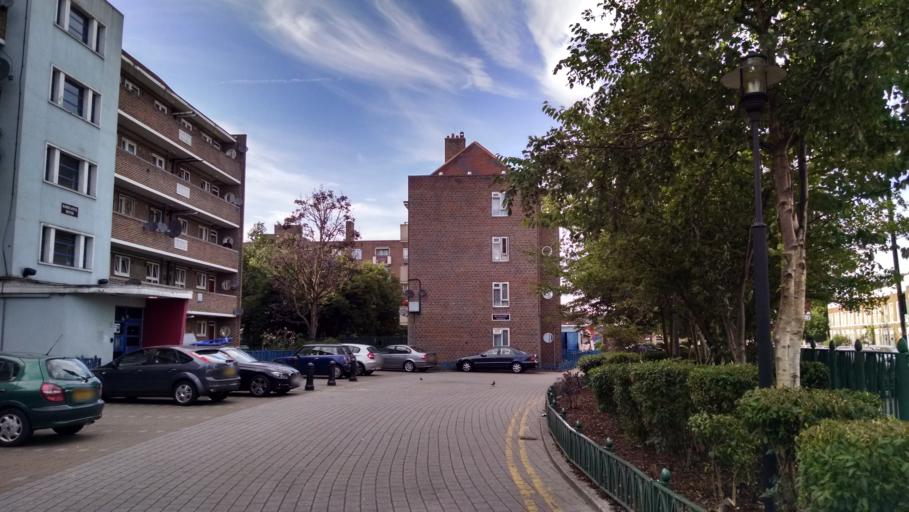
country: GB
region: England
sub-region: Greater London
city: Camberwell
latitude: 51.4744
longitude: -0.0664
